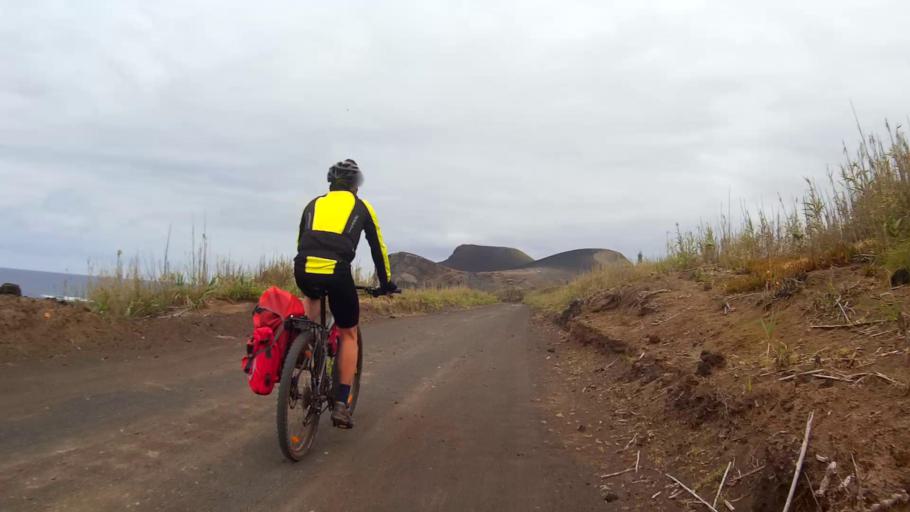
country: PT
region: Azores
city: Ribeira Grande
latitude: 38.5900
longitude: -28.8232
